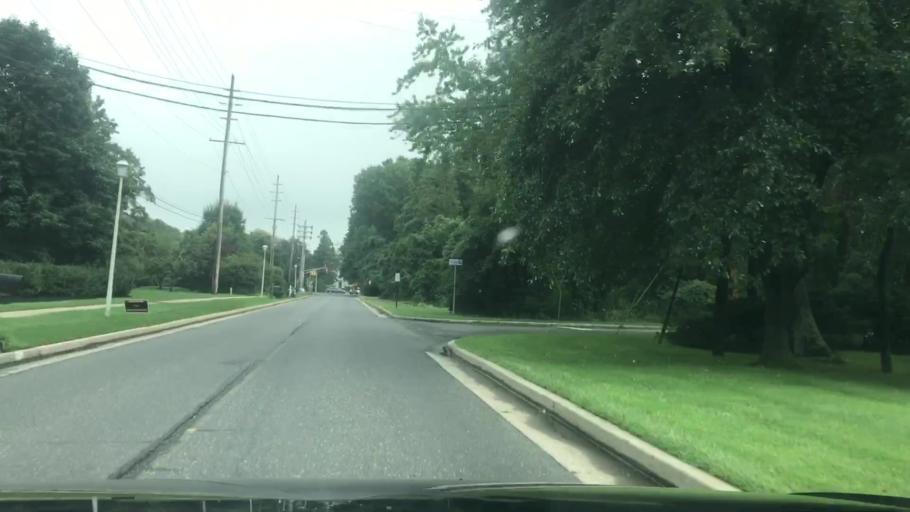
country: US
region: New Jersey
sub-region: Monmouth County
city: Little Silver
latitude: 40.3459
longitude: -74.0383
